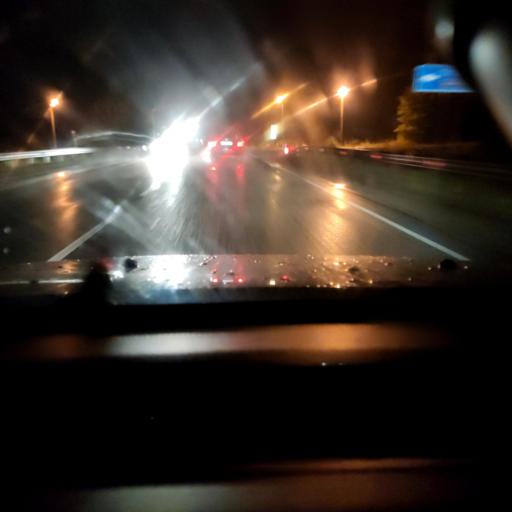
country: RU
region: Udmurtiya
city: Malaya Purga
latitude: 56.5968
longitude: 53.0522
